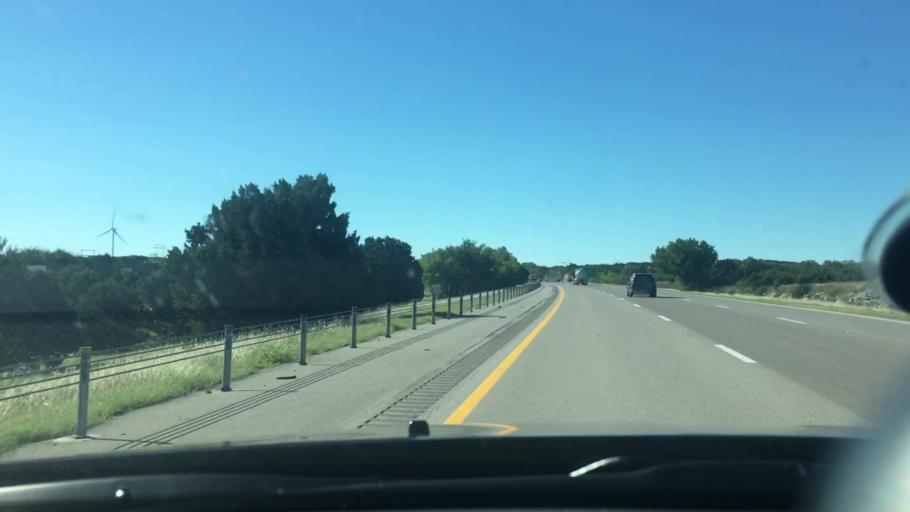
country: US
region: Oklahoma
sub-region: Murray County
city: Davis
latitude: 34.4203
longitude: -97.1362
